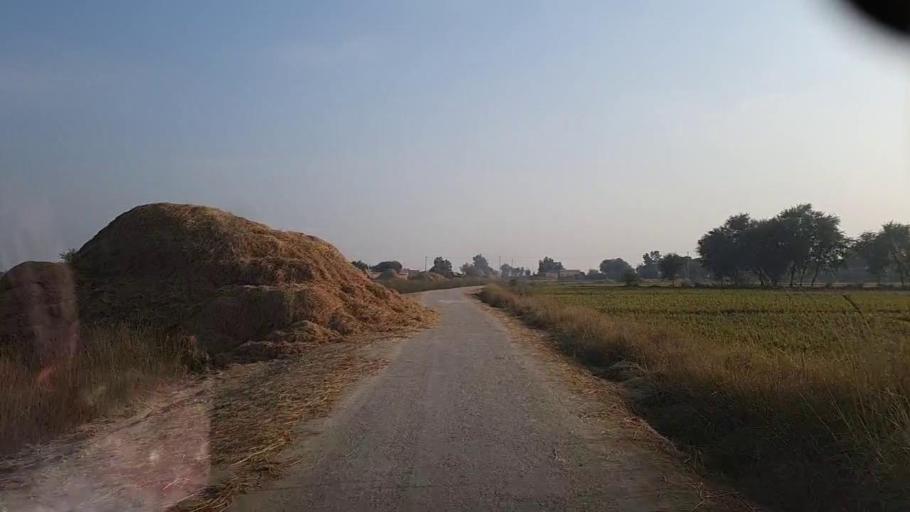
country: PK
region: Sindh
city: Jacobabad
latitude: 28.2336
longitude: 68.4863
